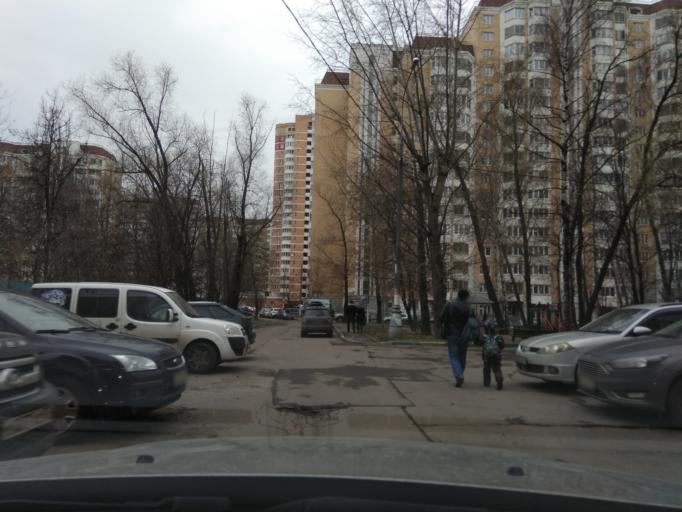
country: RU
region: Moskovskaya
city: Vostochnoe Degunino
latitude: 55.8684
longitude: 37.5600
